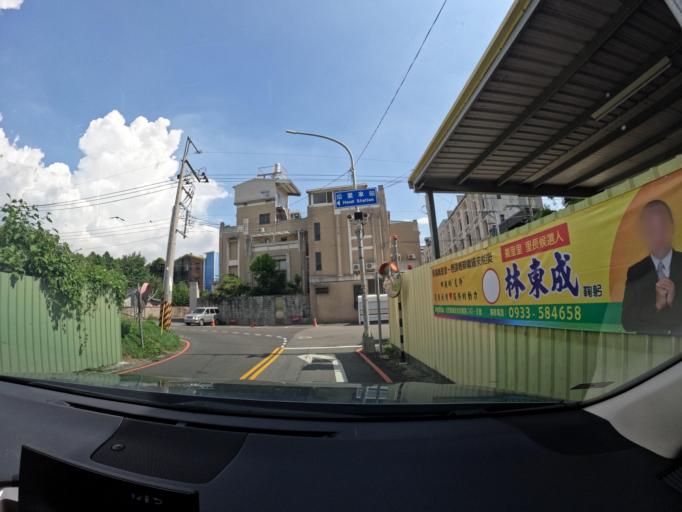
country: TW
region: Taiwan
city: Fengyuan
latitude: 24.3117
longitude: 120.7332
